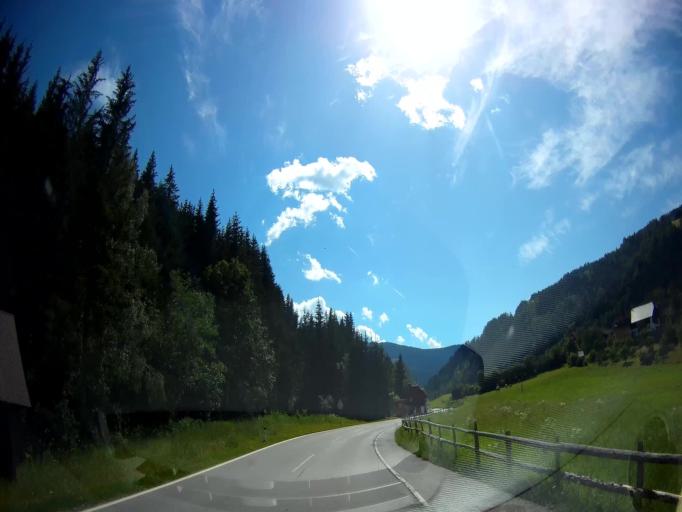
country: AT
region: Salzburg
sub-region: Politischer Bezirk Tamsweg
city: Ramingstein
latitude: 47.0746
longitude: 13.8098
